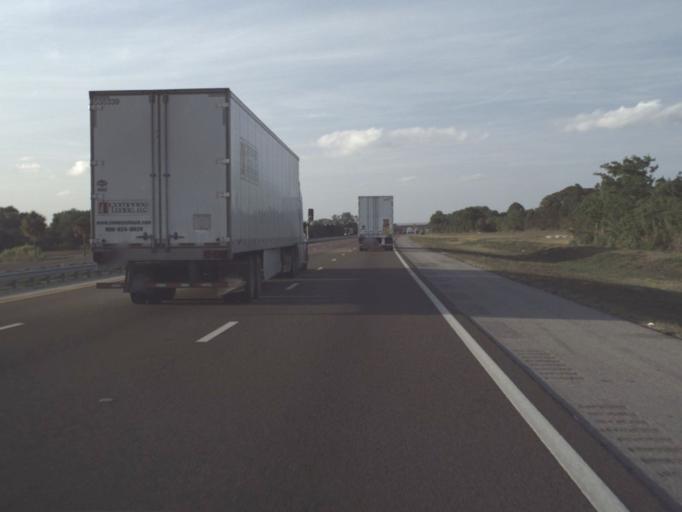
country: US
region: Florida
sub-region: Brevard County
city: Port Saint John
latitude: 28.4547
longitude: -80.8211
